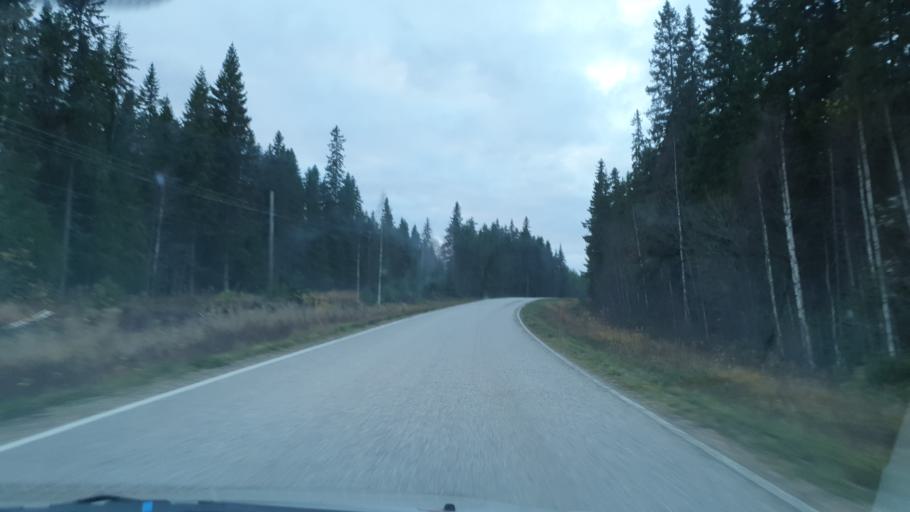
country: FI
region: Kainuu
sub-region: Kajaani
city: Ristijaervi
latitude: 64.4282
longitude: 28.3788
